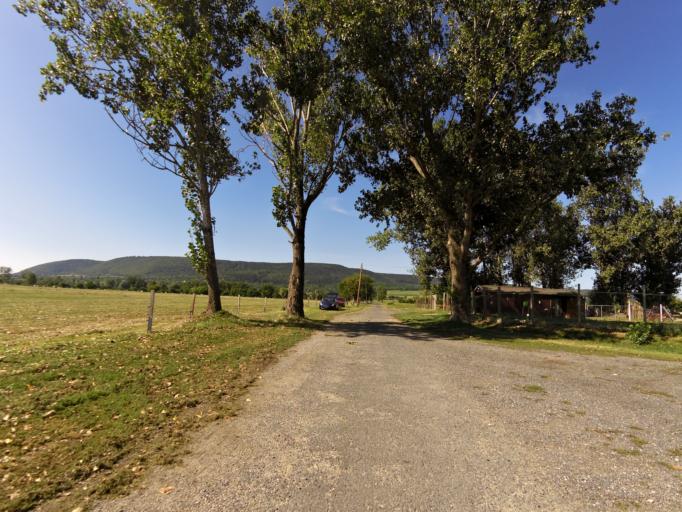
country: HU
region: Veszprem
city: Tapolca
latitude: 46.8329
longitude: 17.3844
